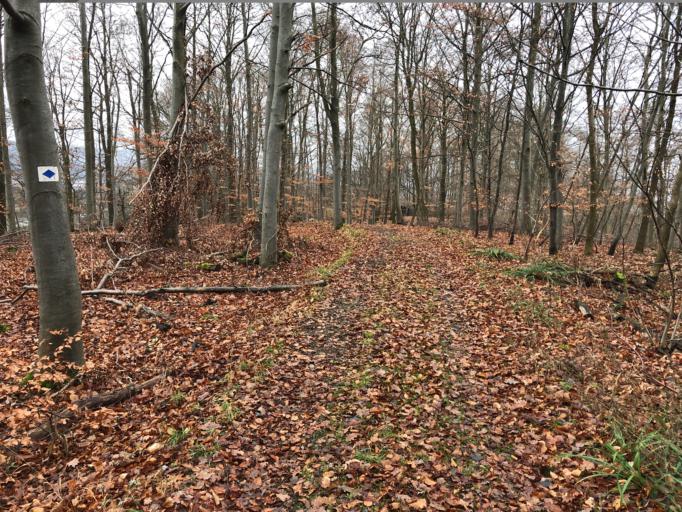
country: DE
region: Baden-Wuerttemberg
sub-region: Tuebingen Region
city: Nehren
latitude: 48.4154
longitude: 9.0772
